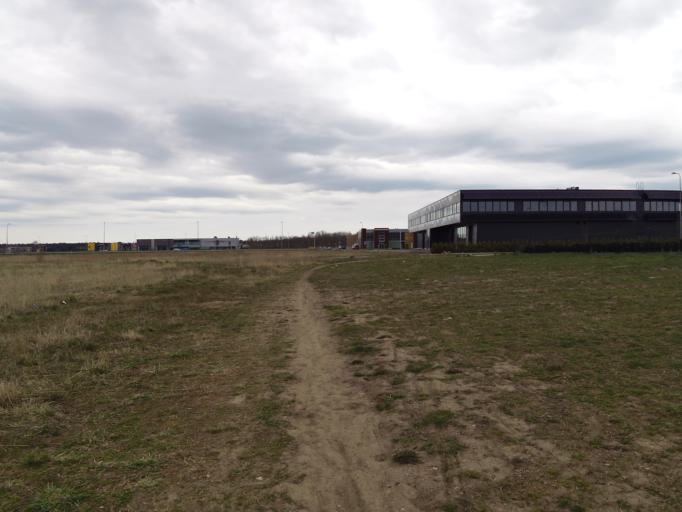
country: EE
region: Harju
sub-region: Tallinna linn
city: Tallinn
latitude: 59.3908
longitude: 24.8203
